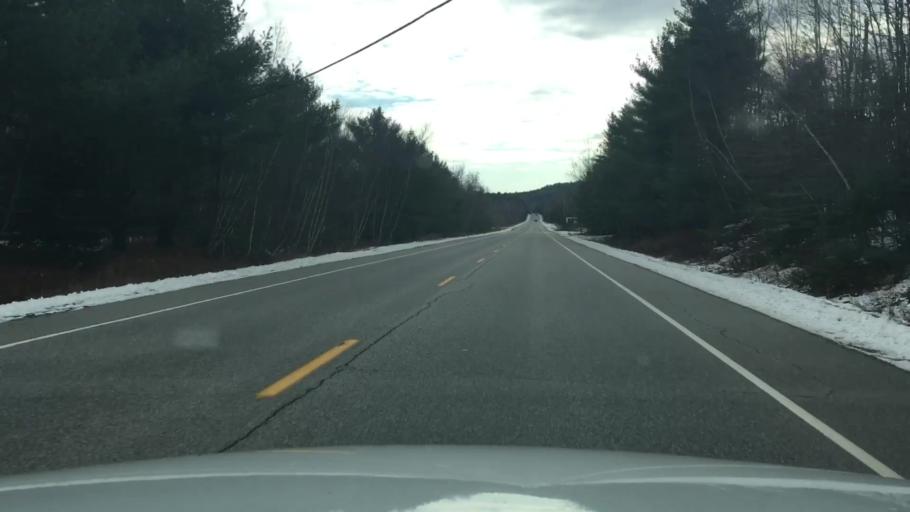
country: US
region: Maine
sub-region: Oxford County
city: Canton
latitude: 44.4313
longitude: -70.3021
